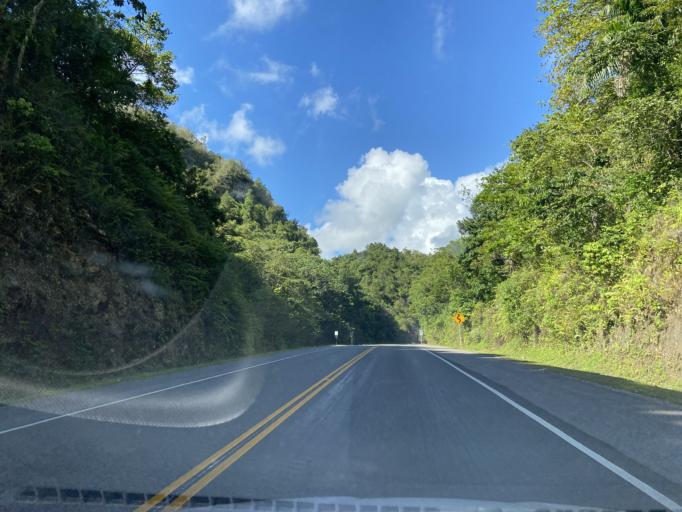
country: DO
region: Monte Plata
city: Majagual
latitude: 19.0722
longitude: -69.8296
